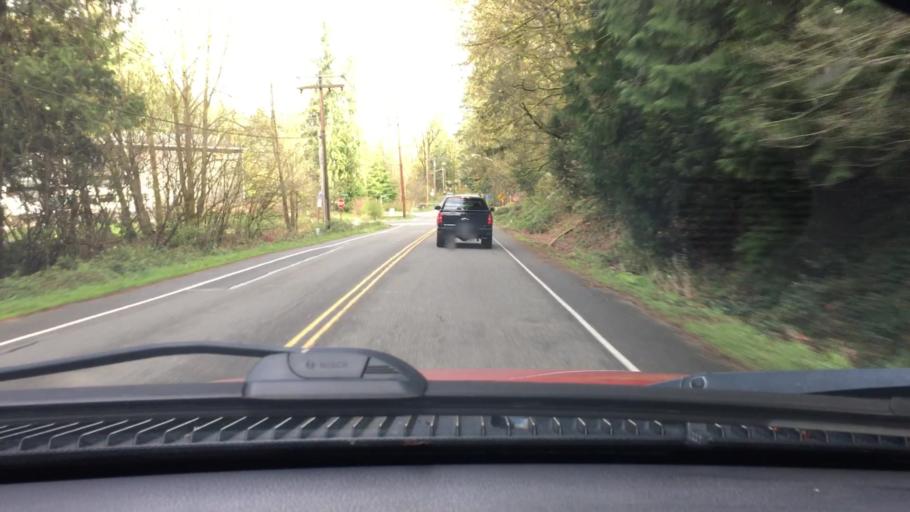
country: US
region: Washington
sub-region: King County
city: Maple Valley
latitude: 47.3727
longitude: -122.0476
